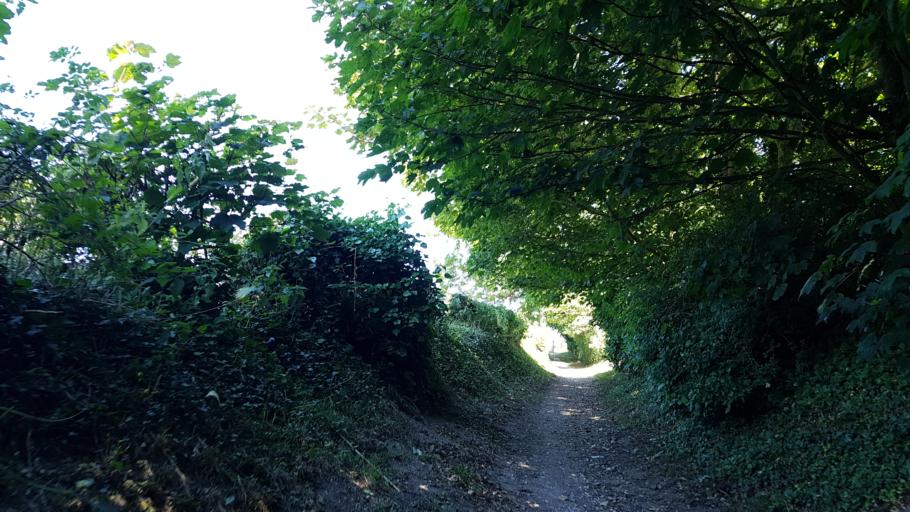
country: GB
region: England
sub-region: Isle of Wight
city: Newport
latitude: 50.6863
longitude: -1.3165
